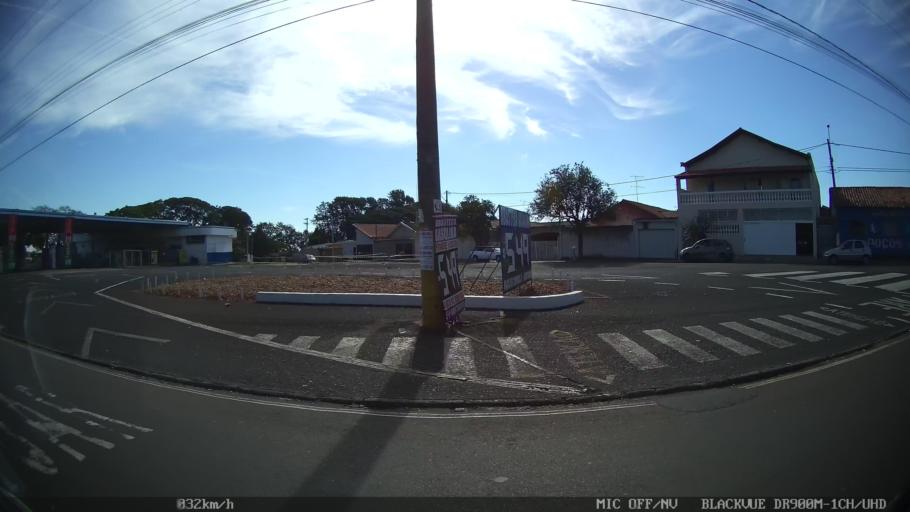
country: BR
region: Sao Paulo
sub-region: Franca
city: Franca
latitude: -20.5402
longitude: -47.4184
